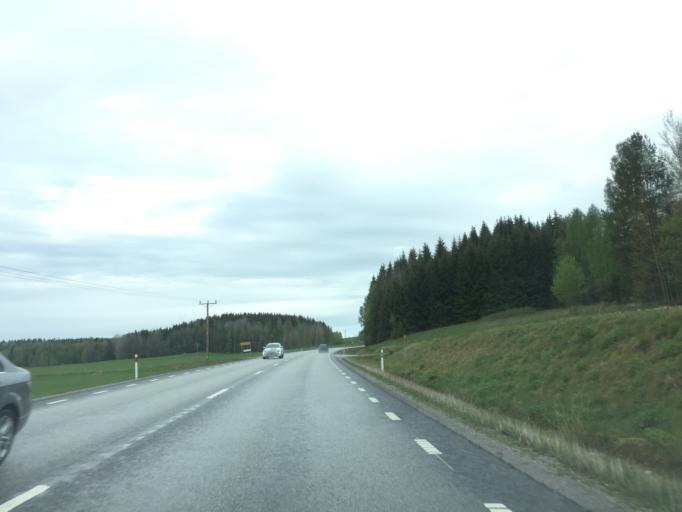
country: SE
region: OErebro
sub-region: Lindesbergs Kommun
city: Lindesberg
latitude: 59.5716
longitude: 15.2079
